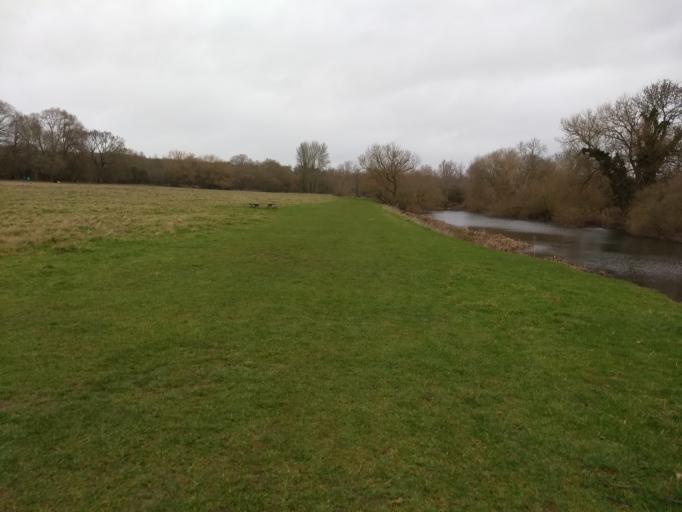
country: GB
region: England
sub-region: Bedford
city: Odell
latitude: 52.2036
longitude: -0.5901
